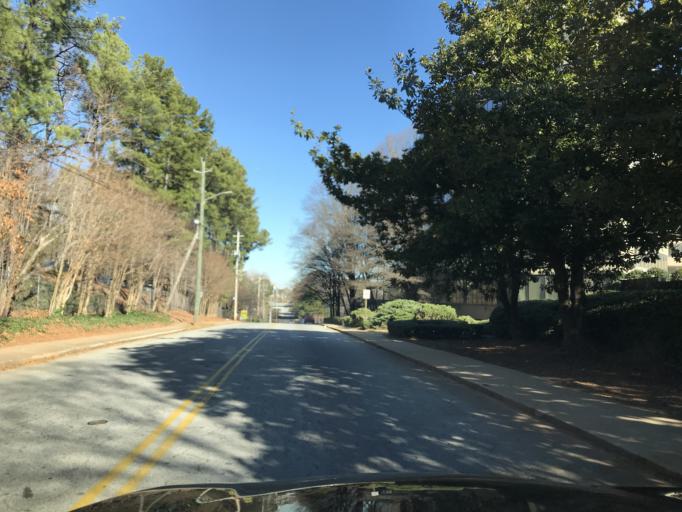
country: US
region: Georgia
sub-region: Fulton County
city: College Park
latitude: 33.6259
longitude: -84.4580
